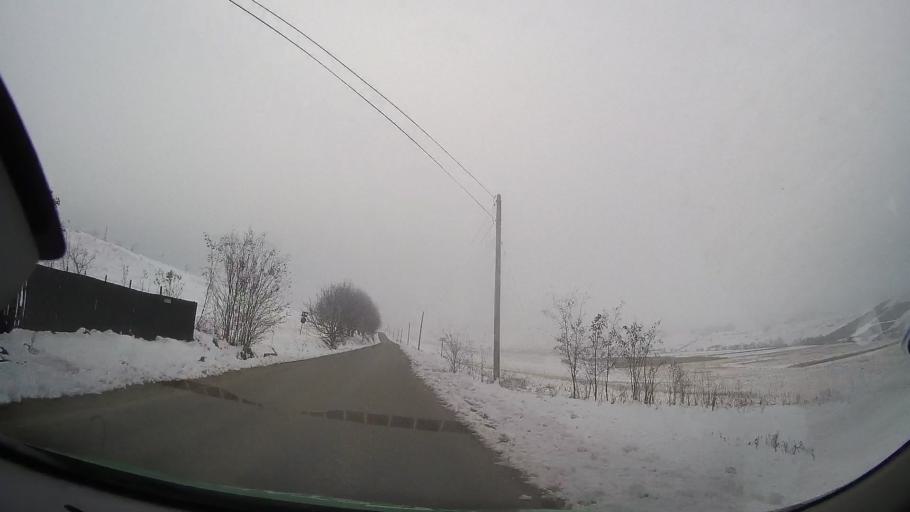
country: RO
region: Bacau
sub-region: Comuna Stanisesti
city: Stanisesti
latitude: 46.4151
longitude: 27.2689
